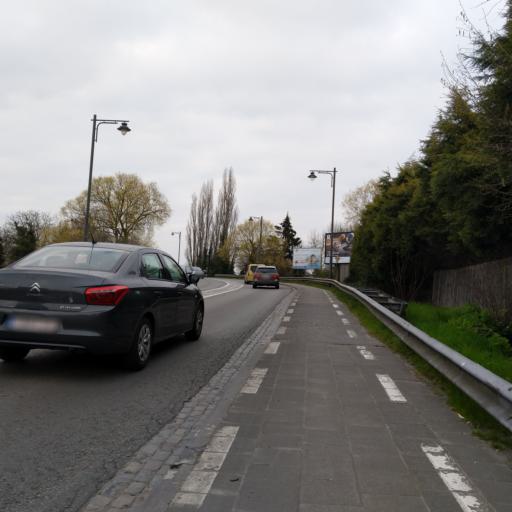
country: BE
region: Wallonia
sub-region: Province du Hainaut
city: Mons
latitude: 50.4711
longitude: 3.9571
